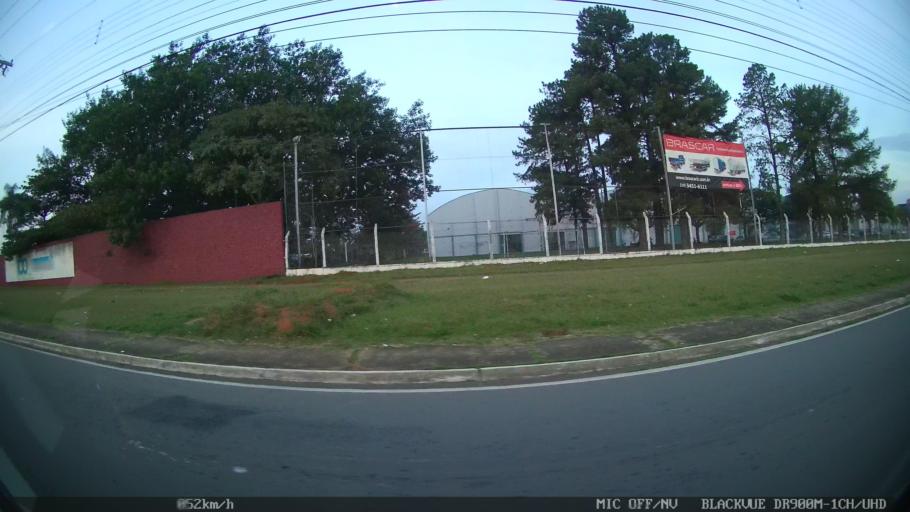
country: BR
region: Sao Paulo
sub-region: Limeira
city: Limeira
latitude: -22.5504
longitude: -47.3791
